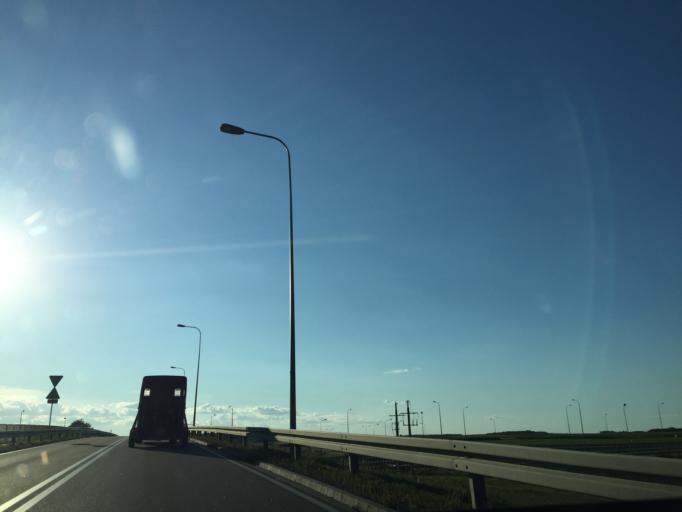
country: PL
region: Podlasie
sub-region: Powiat kolnenski
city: Stawiski
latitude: 53.3862
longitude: 22.1458
